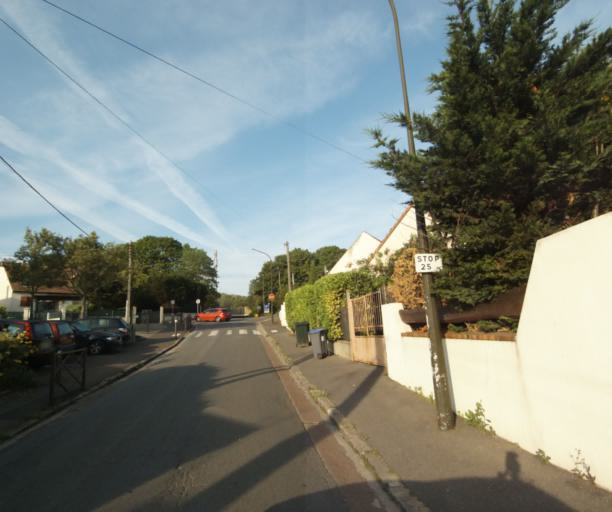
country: FR
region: Ile-de-France
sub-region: Departement du Val-d'Oise
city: Saint-Gratien
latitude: 48.9628
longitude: 2.2704
